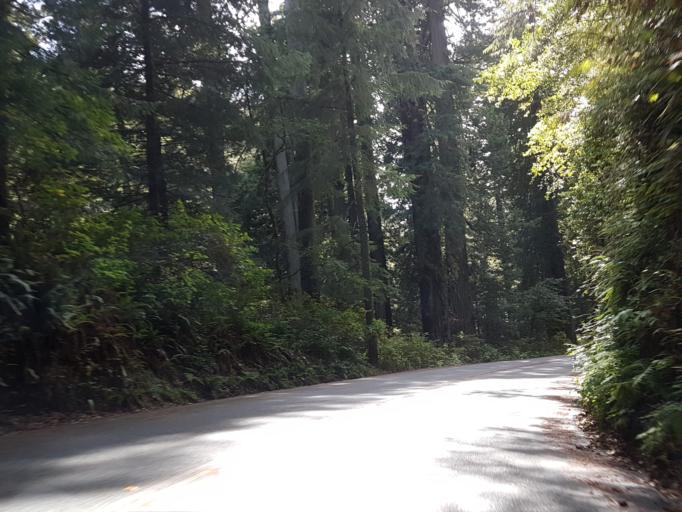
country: US
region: California
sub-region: Del Norte County
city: Bertsch-Oceanview
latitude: 41.4470
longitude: -124.0400
